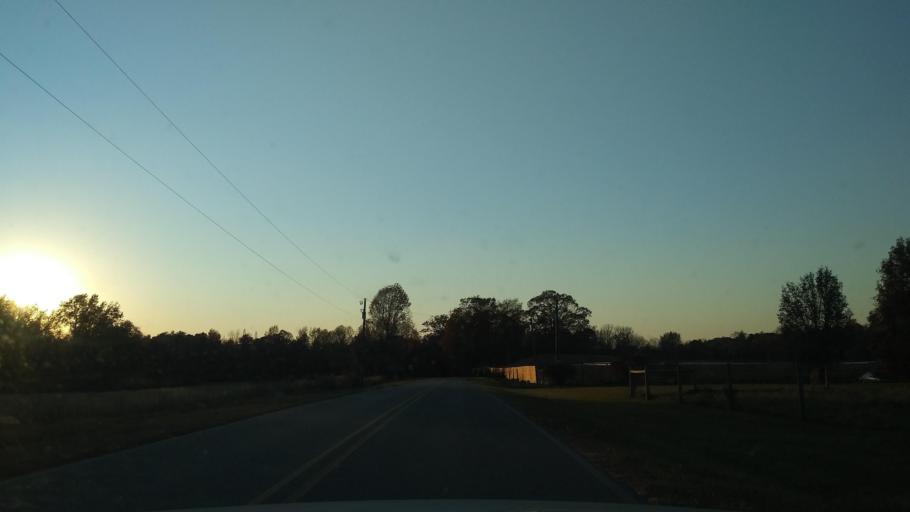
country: US
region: North Carolina
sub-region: Guilford County
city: Pleasant Garden
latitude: 36.0009
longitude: -79.7744
